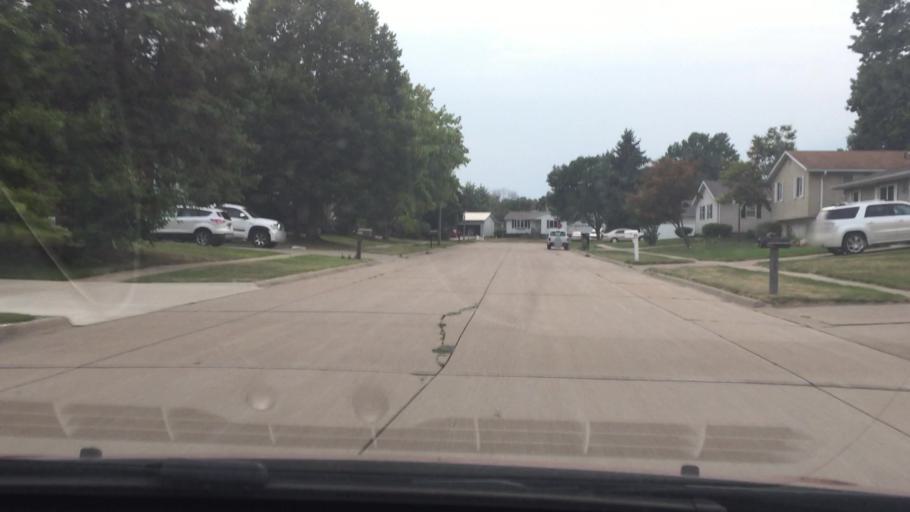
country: US
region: Iowa
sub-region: Muscatine County
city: Muscatine
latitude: 41.4427
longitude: -91.0534
